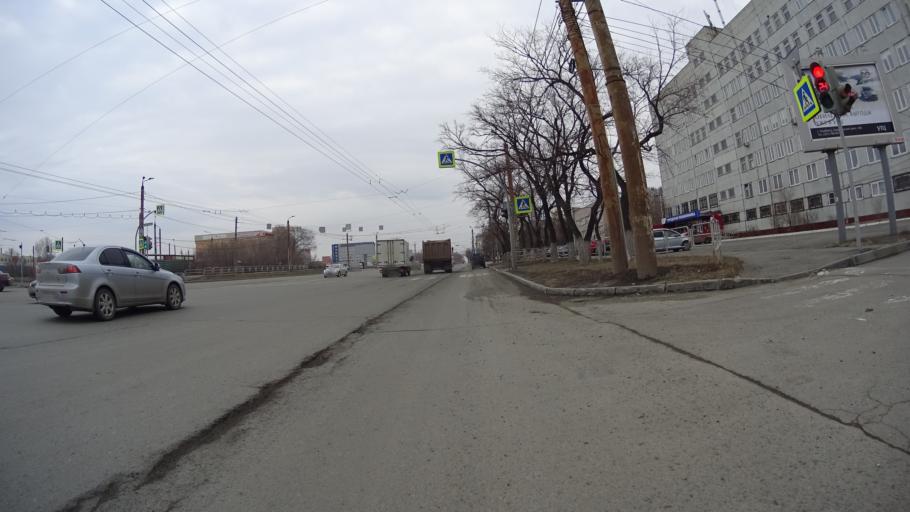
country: RU
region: Chelyabinsk
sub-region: Gorod Chelyabinsk
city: Chelyabinsk
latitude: 55.1592
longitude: 61.4653
